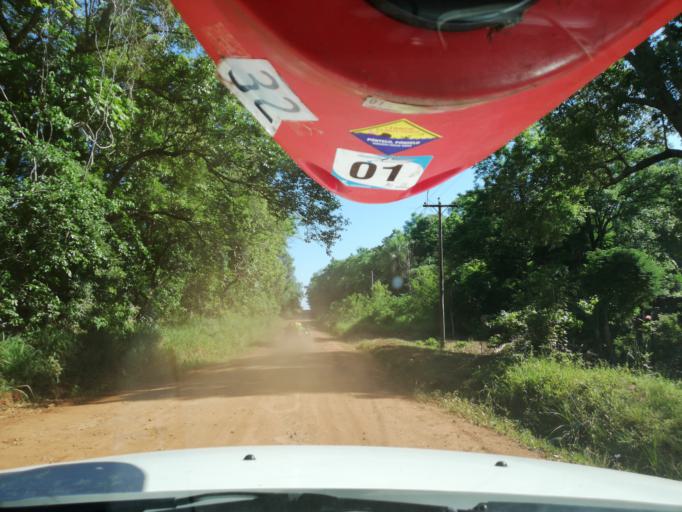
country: AR
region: Misiones
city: Puerto Leoni
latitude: -26.9795
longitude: -55.1647
